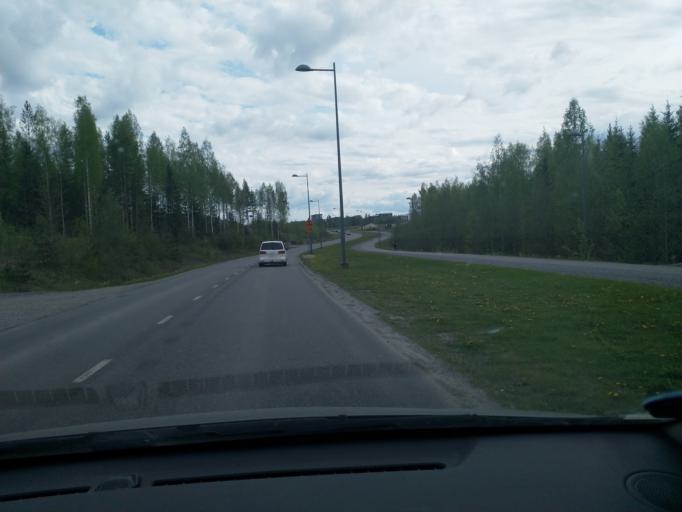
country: FI
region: Pirkanmaa
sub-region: Tampere
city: Tampere
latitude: 61.4470
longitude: 23.8065
